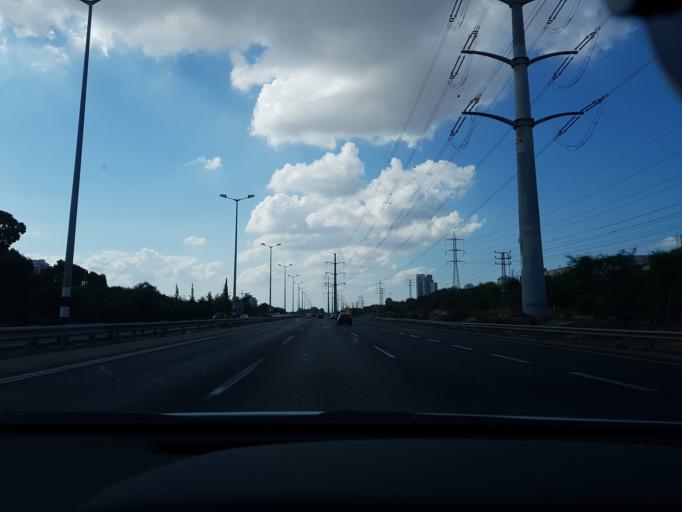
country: IL
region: Central District
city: Rishon LeZiyyon
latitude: 31.9836
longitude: 34.7949
